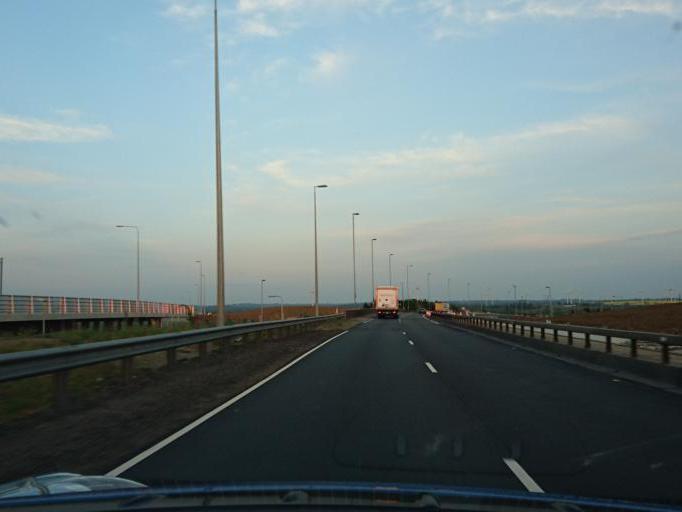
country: GB
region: England
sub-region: Leicestershire
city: Lutterworth
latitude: 52.4040
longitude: -1.1773
